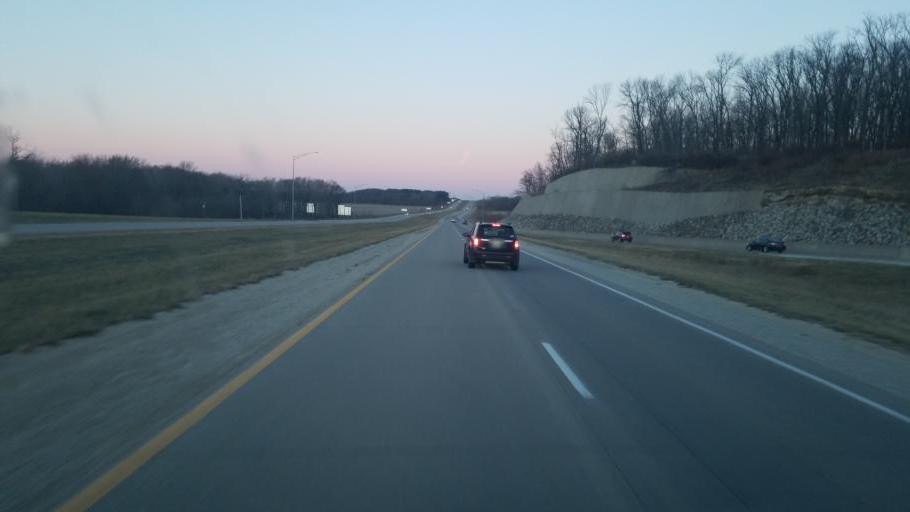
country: US
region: Iowa
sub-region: Henry County
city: Mount Pleasant
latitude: 40.9697
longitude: -91.6367
